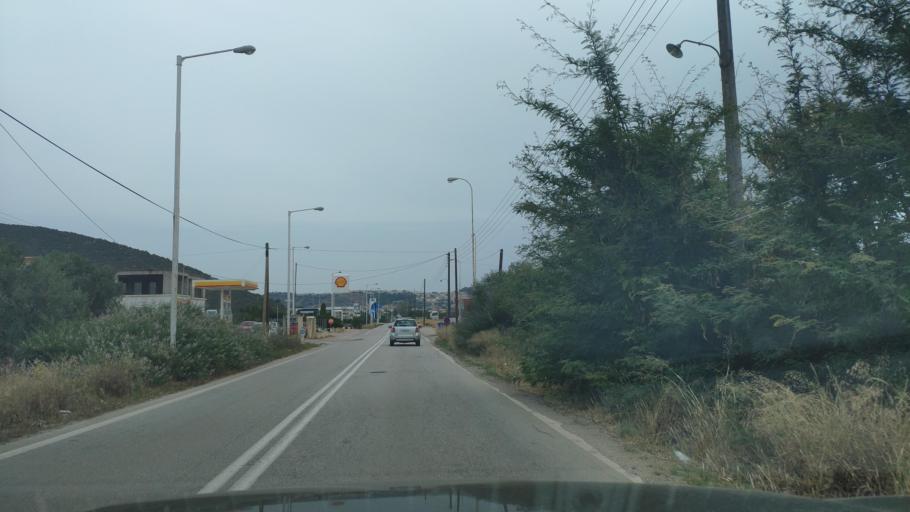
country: GR
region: Peloponnese
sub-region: Nomos Argolidos
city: Kranidi
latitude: 37.4040
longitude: 23.1550
